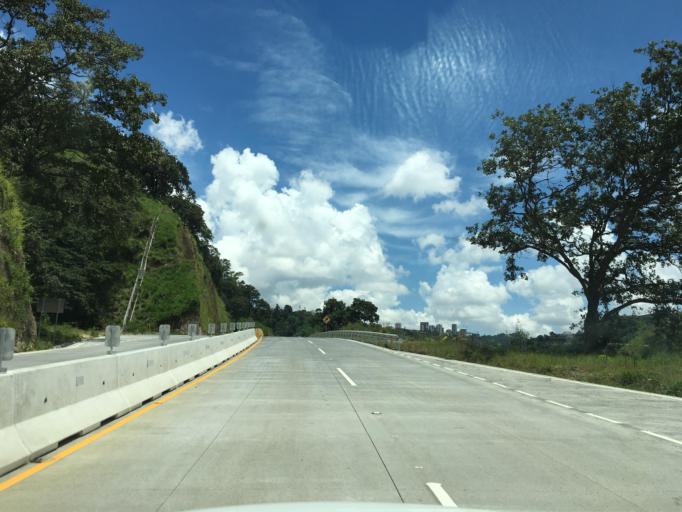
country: GT
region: Guatemala
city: Santa Catarina Pinula
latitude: 14.5468
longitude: -90.5320
